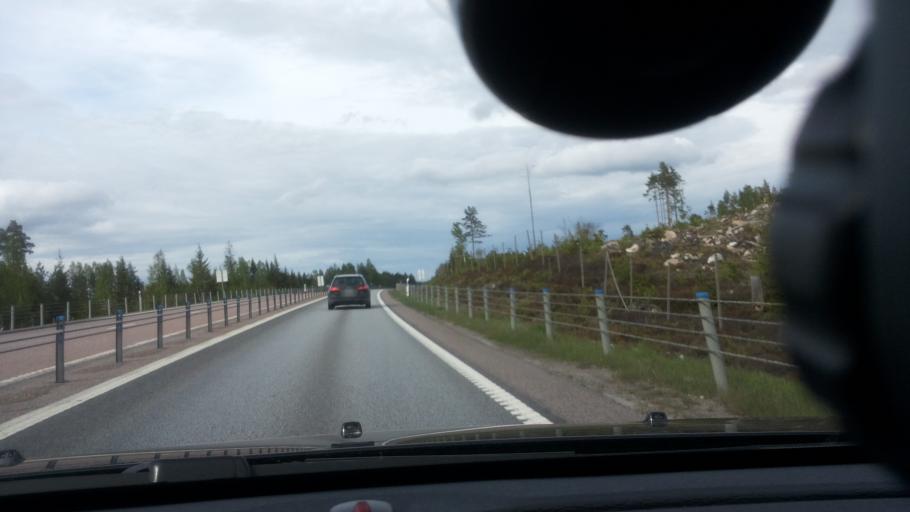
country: SE
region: Gaevleborg
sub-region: Soderhamns Kommun
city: Ljusne
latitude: 61.0974
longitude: 16.9864
